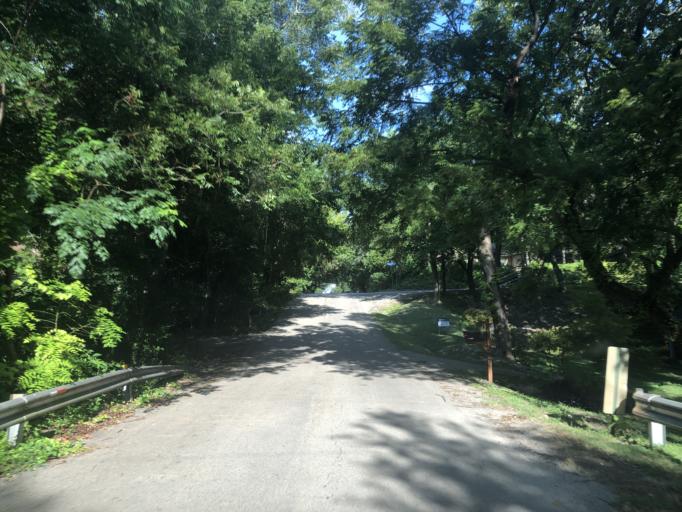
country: US
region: Texas
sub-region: Dallas County
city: Duncanville
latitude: 32.6651
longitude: -96.9227
